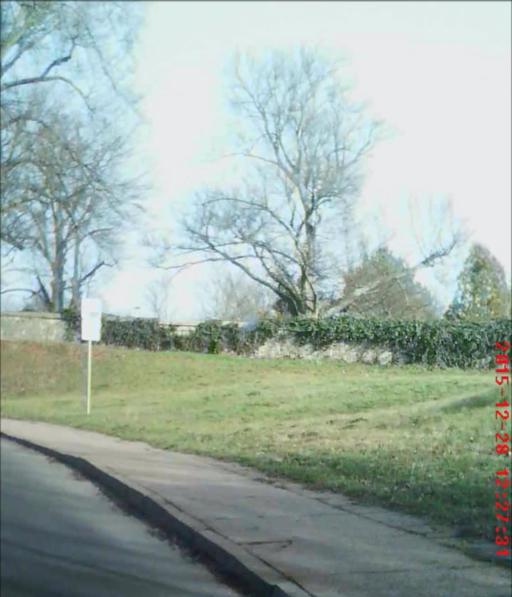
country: DE
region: Thuringia
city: Ossmanstedt
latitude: 51.0151
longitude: 11.4244
